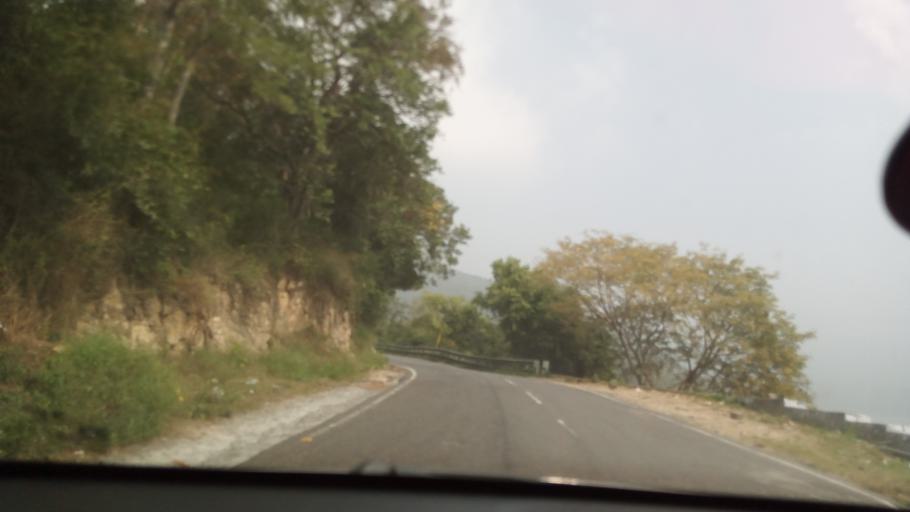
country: IN
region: Tamil Nadu
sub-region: Erode
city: Sathyamangalam
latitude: 11.5944
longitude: 77.1256
